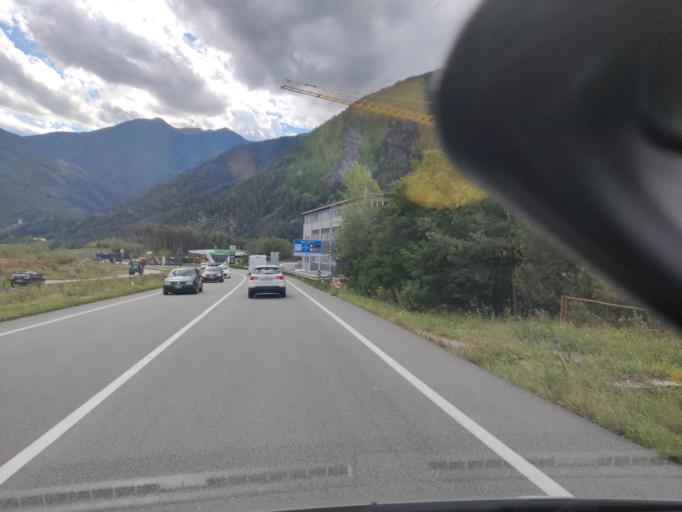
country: IT
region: Trentino-Alto Adige
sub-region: Bolzano
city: Varna
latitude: 46.7609
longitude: 11.6398
